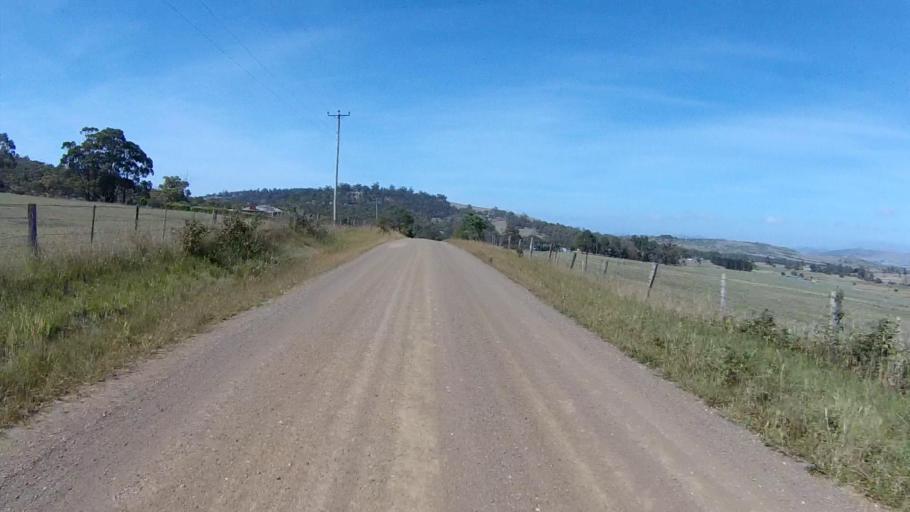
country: AU
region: Tasmania
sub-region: Sorell
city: Sorell
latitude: -42.7276
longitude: 147.5966
